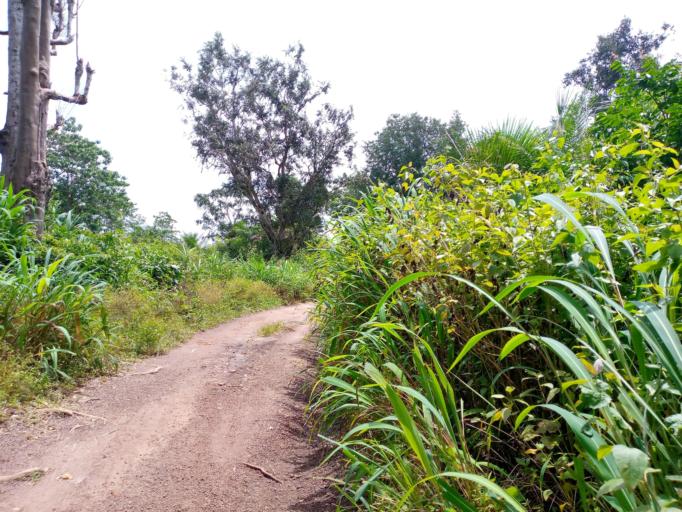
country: SL
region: Northern Province
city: Magburaka
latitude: 8.7261
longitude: -11.9272
